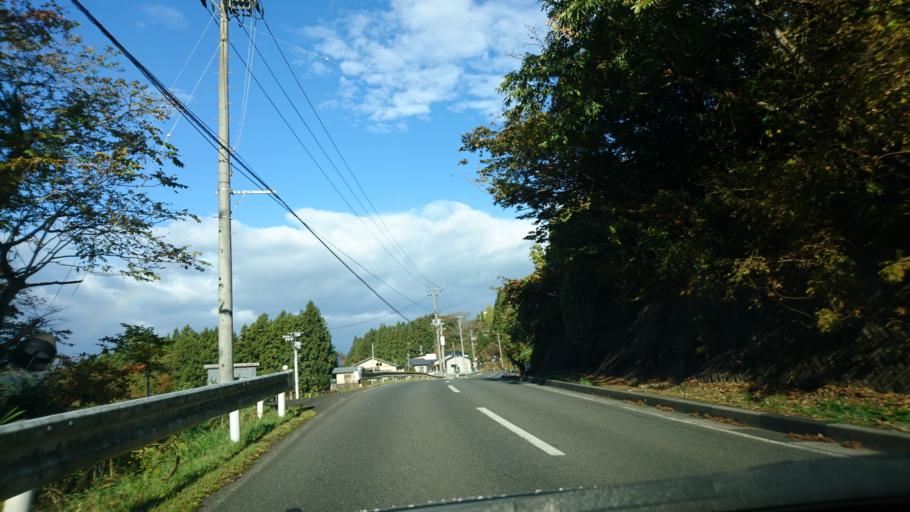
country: JP
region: Iwate
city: Mizusawa
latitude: 39.0371
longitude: 141.0705
